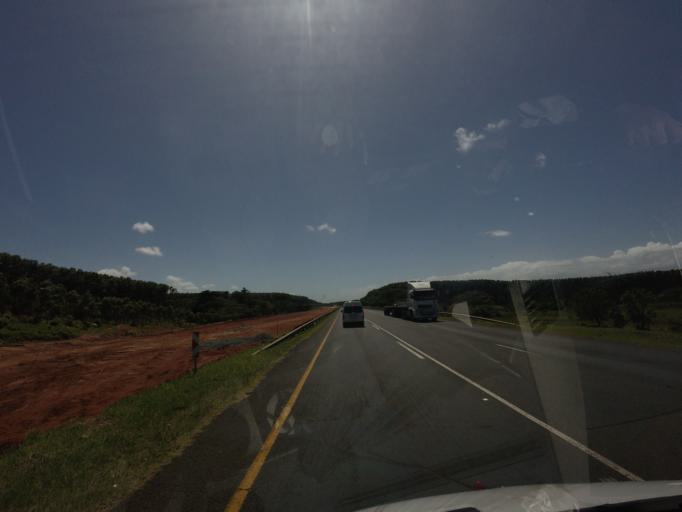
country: ZA
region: KwaZulu-Natal
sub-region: uThungulu District Municipality
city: eSikhawini
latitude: -28.8895
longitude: 31.8479
